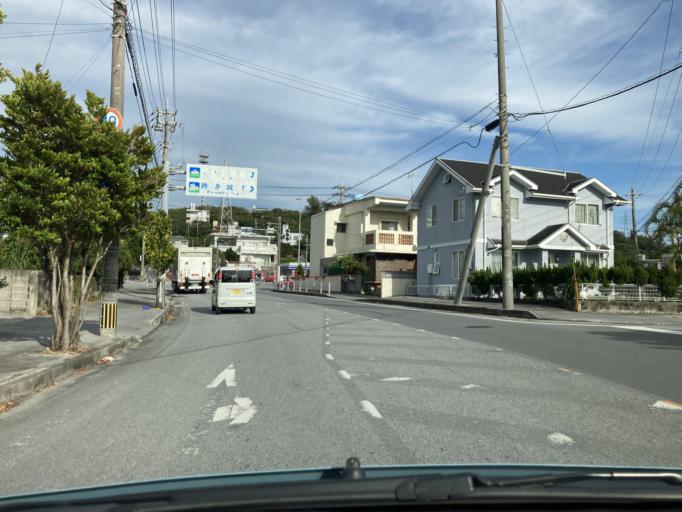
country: JP
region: Okinawa
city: Katsuren-haebaru
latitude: 26.3448
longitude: 127.8667
